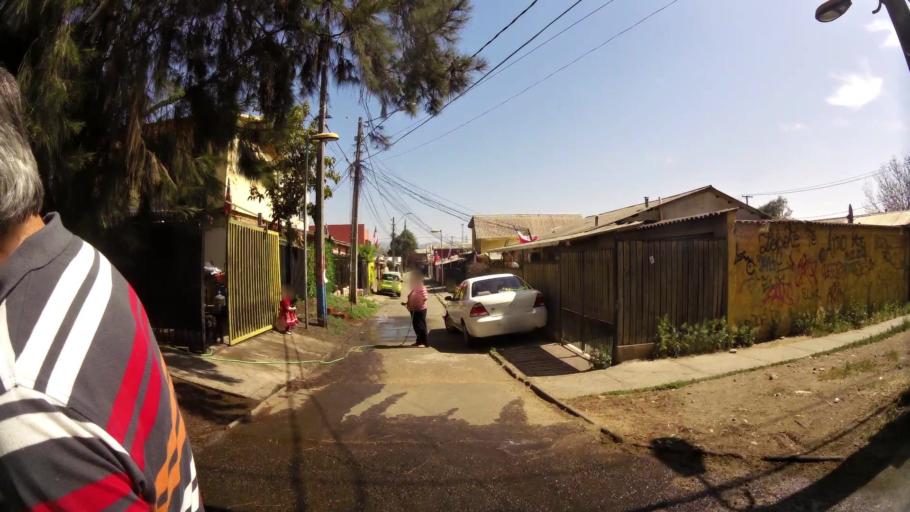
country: CL
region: Santiago Metropolitan
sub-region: Provincia de Santiago
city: Lo Prado
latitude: -33.4913
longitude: -70.7431
